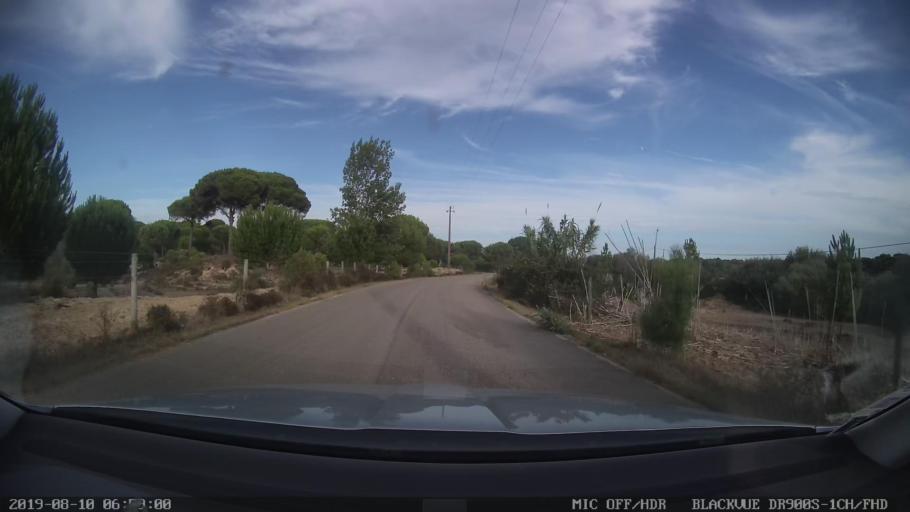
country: PT
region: Santarem
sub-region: Benavente
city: Poceirao
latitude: 38.8470
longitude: -8.7112
